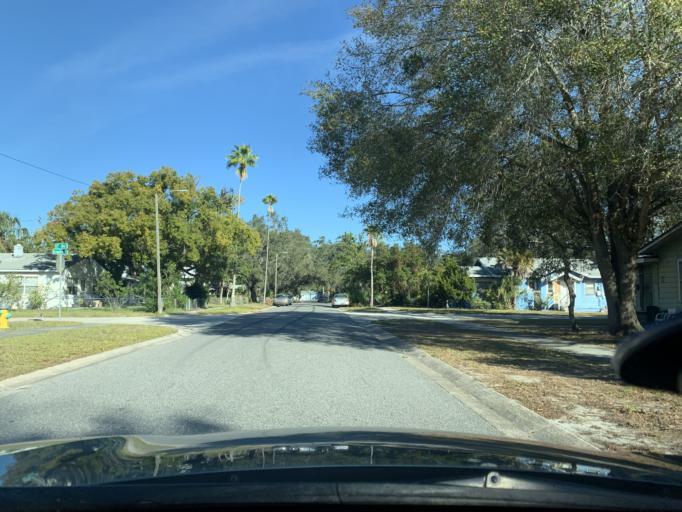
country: US
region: Florida
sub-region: Pinellas County
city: Gulfport
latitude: 27.7534
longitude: -82.6951
